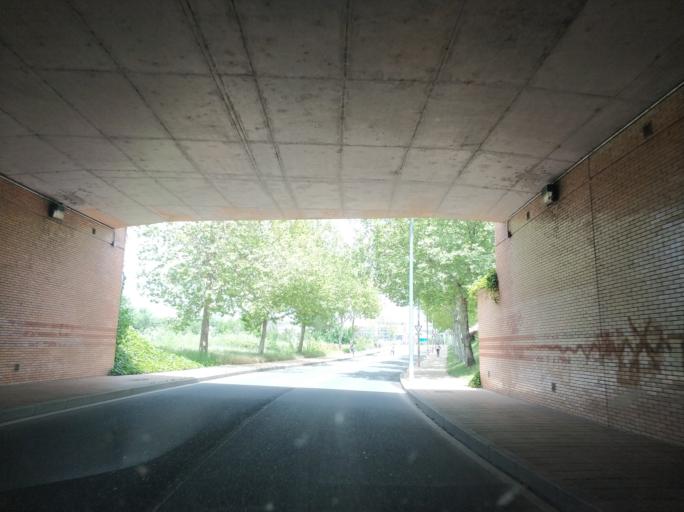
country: ES
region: Castille and Leon
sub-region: Provincia de Salamanca
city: Salamanca
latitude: 40.9533
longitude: -5.6912
